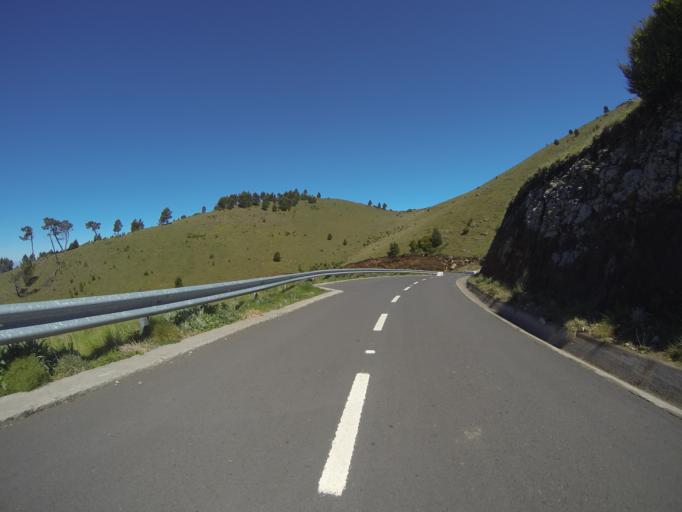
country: PT
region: Madeira
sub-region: Camara de Lobos
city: Curral das Freiras
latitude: 32.7122
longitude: -16.9553
